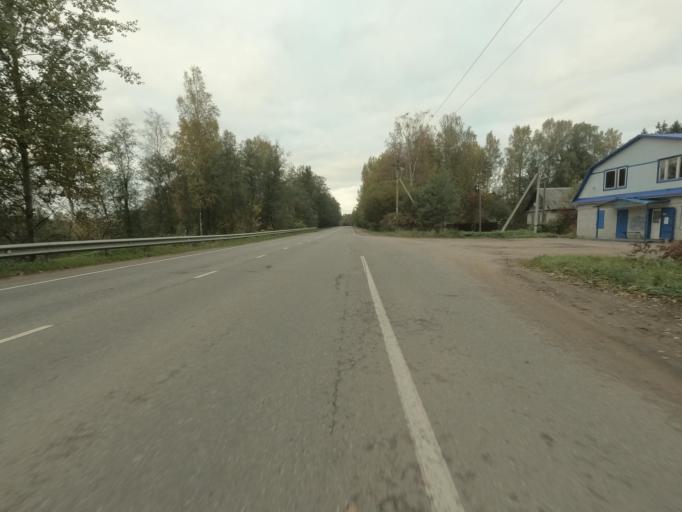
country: RU
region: Leningrad
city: Pavlovo
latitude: 59.7831
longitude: 30.9706
